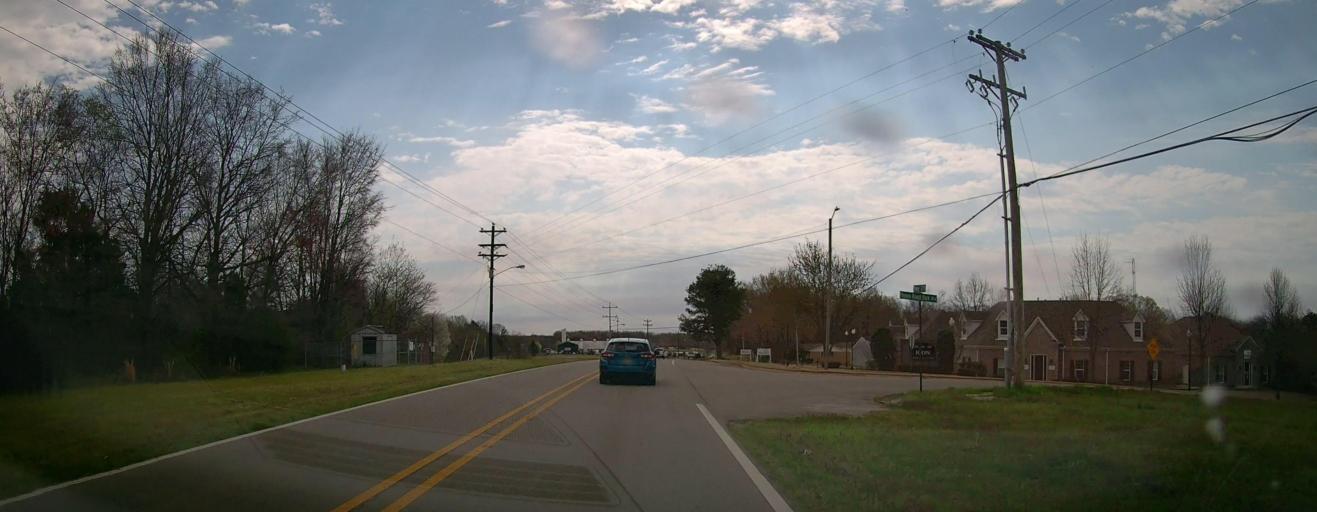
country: US
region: Mississippi
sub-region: De Soto County
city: Olive Branch
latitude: 34.9551
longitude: -89.8162
